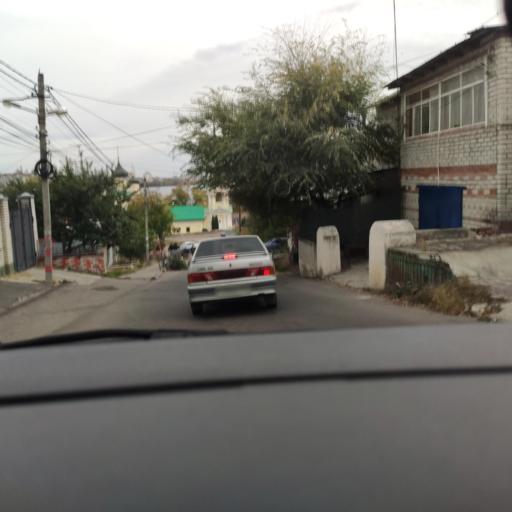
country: RU
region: Voronezj
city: Voronezh
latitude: 51.6579
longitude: 39.2127
